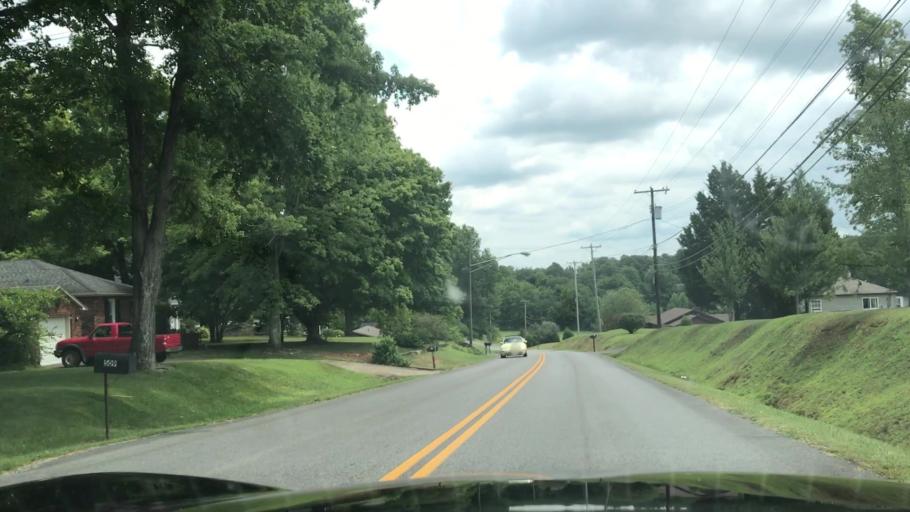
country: US
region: Kentucky
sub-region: Muhlenberg County
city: Greenville
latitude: 37.2046
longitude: -87.1667
